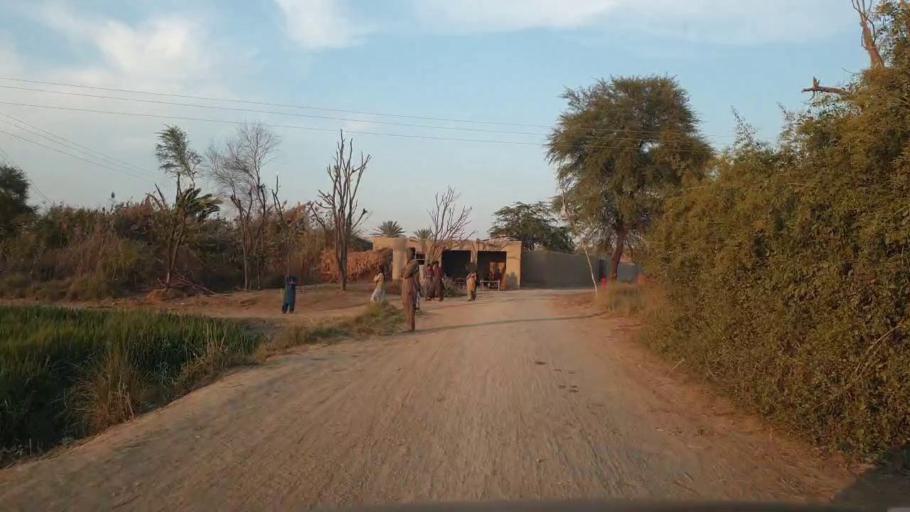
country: PK
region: Sindh
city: Shahpur Chakar
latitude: 26.1994
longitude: 68.6199
